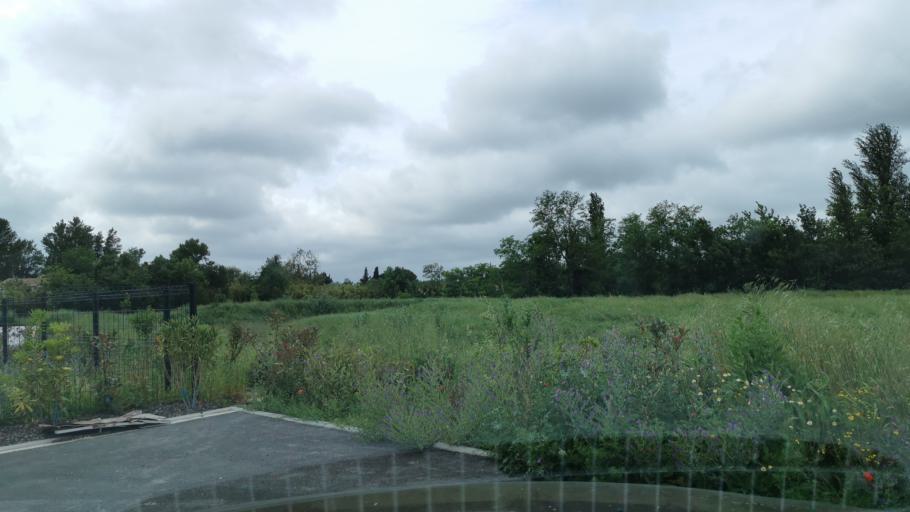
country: FR
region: Languedoc-Roussillon
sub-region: Departement de l'Aude
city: Narbonne
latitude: 43.1964
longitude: 3.0078
